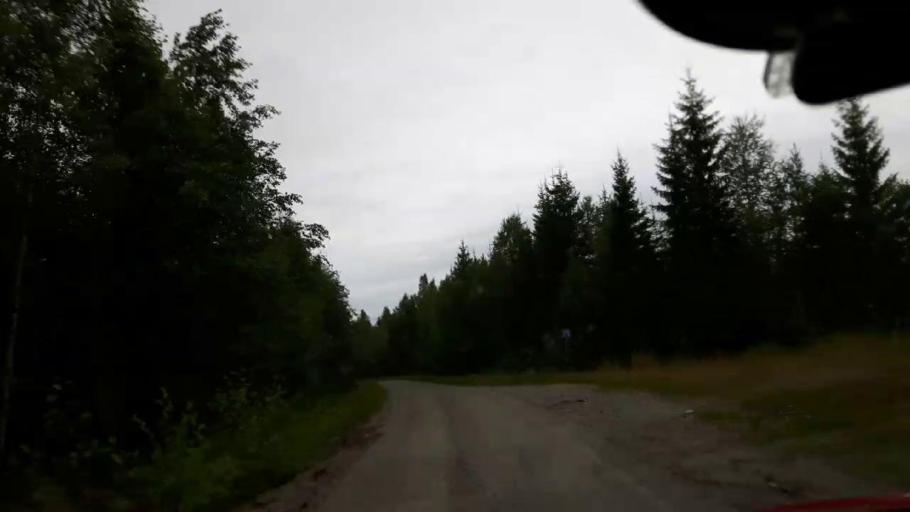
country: SE
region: Vaesternorrland
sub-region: Ange Kommun
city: Ange
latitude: 62.7847
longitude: 15.7735
